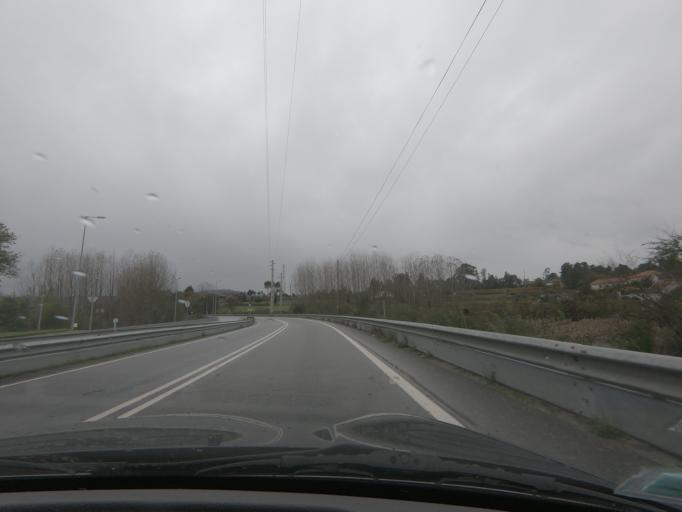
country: PT
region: Porto
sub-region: Amarante
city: Amarante
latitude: 41.3033
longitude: -8.0803
